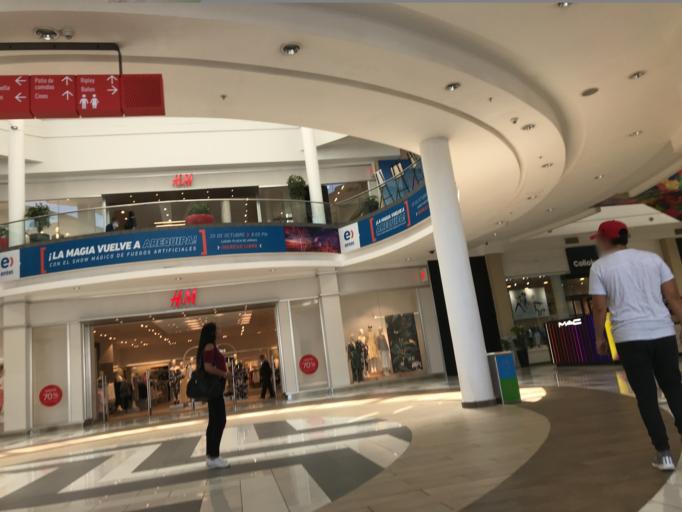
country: PE
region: Arequipa
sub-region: Provincia de Arequipa
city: Arequipa
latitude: -16.4175
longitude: -71.5139
